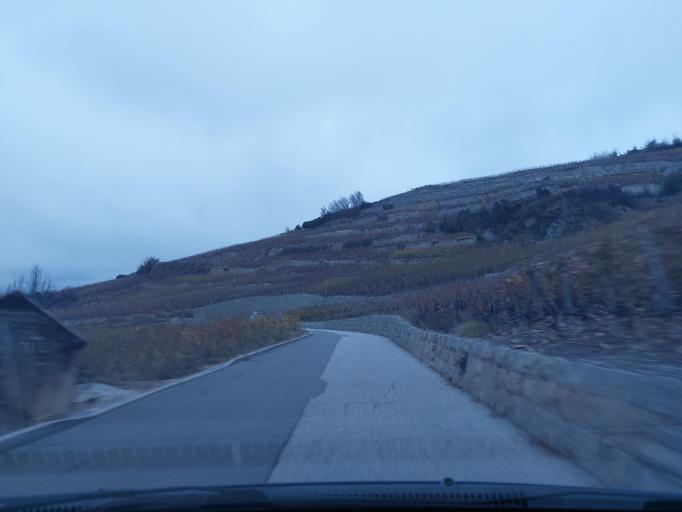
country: CH
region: Valais
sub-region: Conthey District
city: Conthey
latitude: 46.2354
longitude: 7.3189
